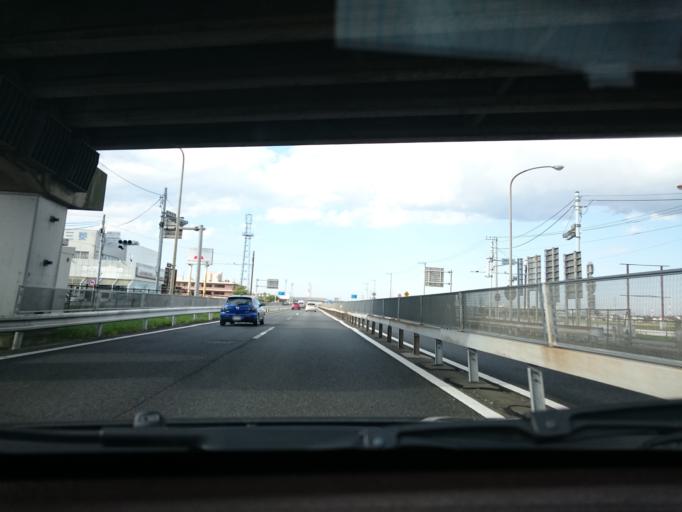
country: JP
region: Kanagawa
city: Isehara
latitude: 35.3863
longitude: 139.3314
